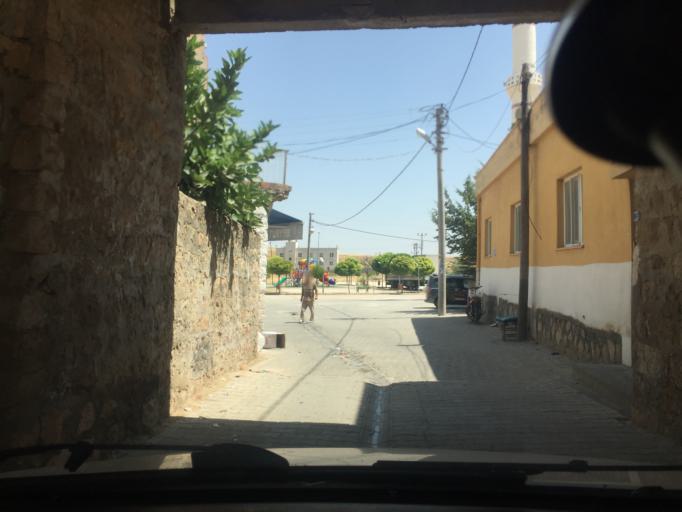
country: TR
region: Mardin
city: Kindirip
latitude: 37.4454
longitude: 41.2215
